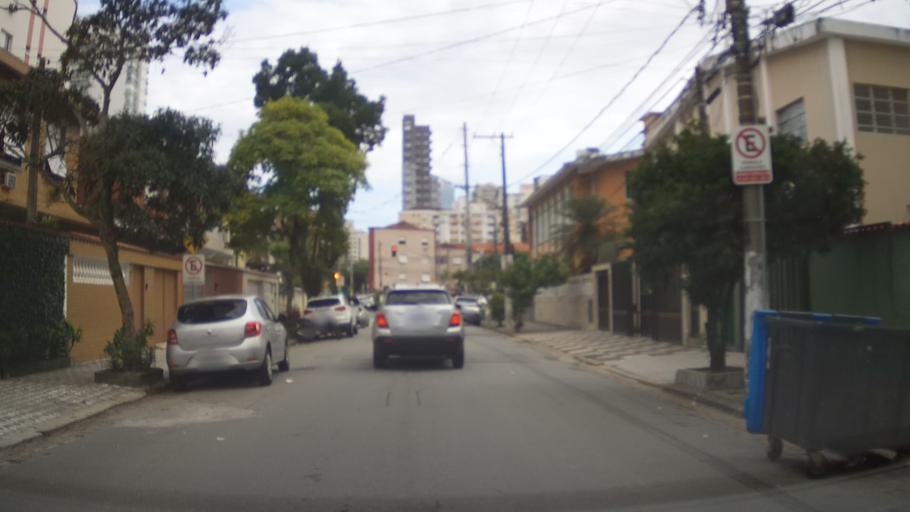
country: BR
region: Sao Paulo
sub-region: Santos
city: Santos
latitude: -23.9614
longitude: -46.3407
